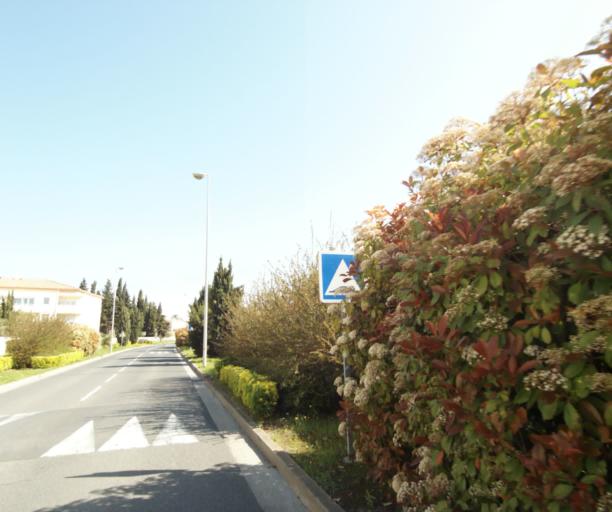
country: FR
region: Languedoc-Roussillon
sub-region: Departement de l'Herault
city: Lattes
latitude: 43.5743
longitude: 3.9060
